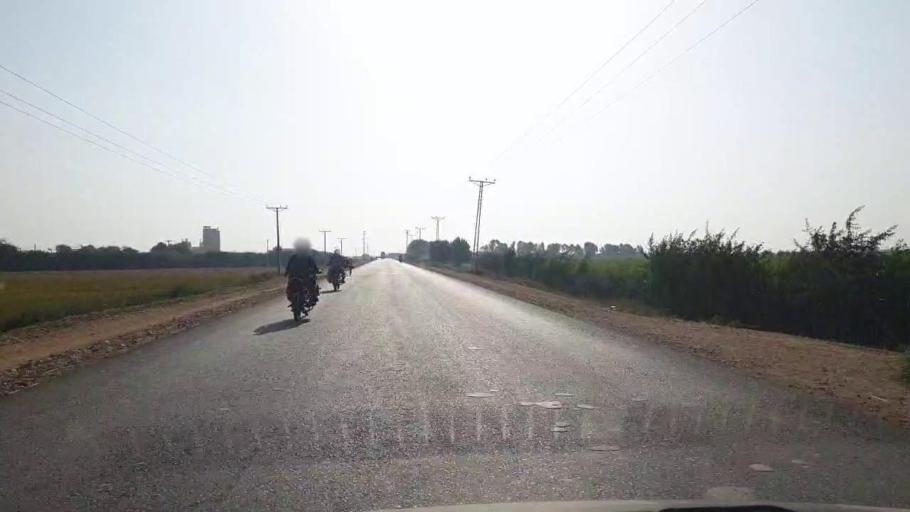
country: PK
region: Sindh
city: Badin
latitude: 24.6626
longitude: 68.8753
